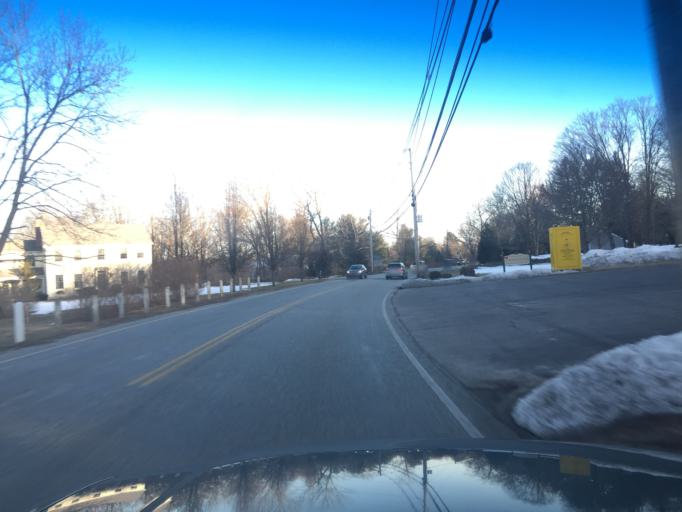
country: US
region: Massachusetts
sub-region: Worcester County
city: Mendon
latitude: 42.1018
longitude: -71.5435
